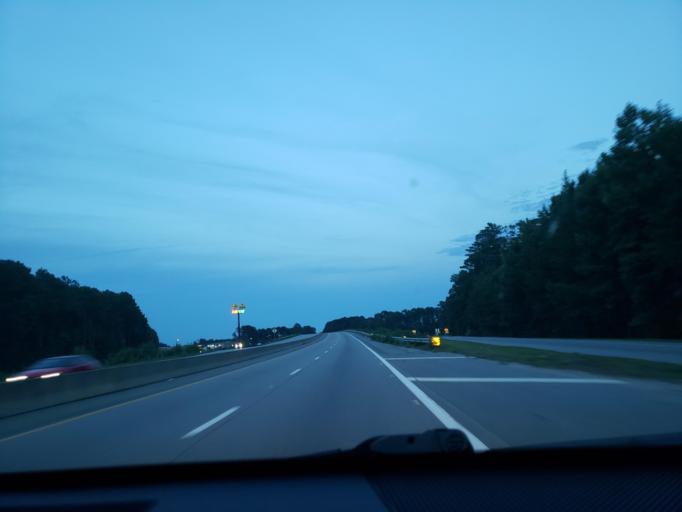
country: US
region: Virginia
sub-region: City of Franklin
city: Franklin
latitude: 36.6618
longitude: -76.9471
